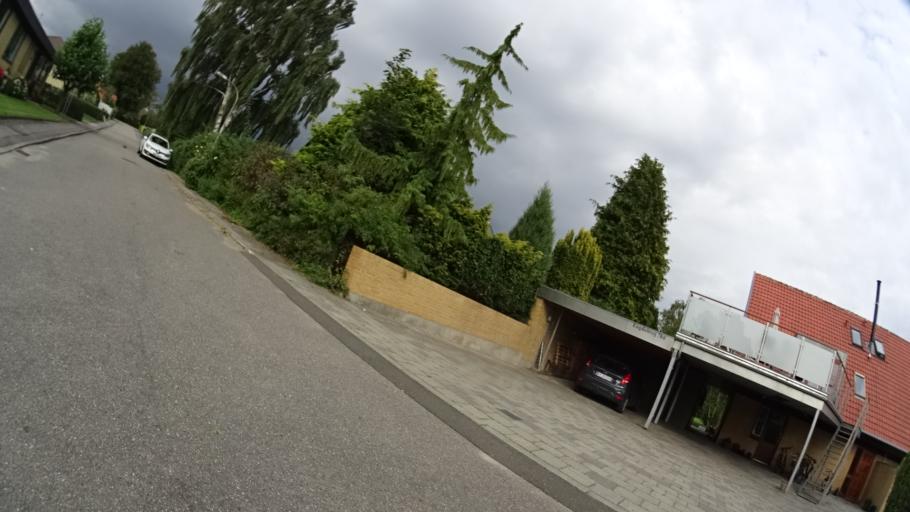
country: DK
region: Central Jutland
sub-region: Arhus Kommune
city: Stavtrup
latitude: 56.1499
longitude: 10.1154
